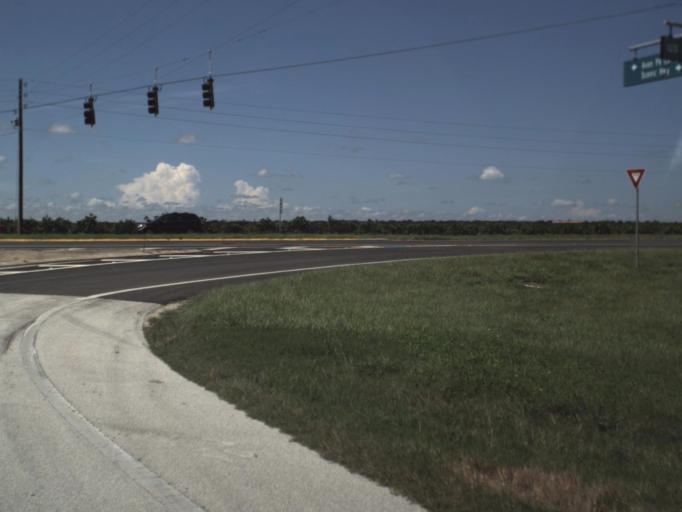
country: US
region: Florida
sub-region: Polk County
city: Frostproof
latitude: 27.6784
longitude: -81.5534
